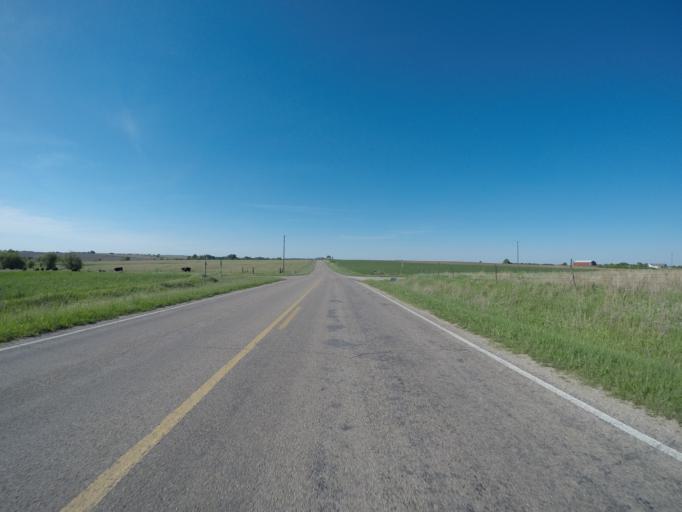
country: US
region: Kansas
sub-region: Clay County
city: Clay Center
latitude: 39.3938
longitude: -96.9980
